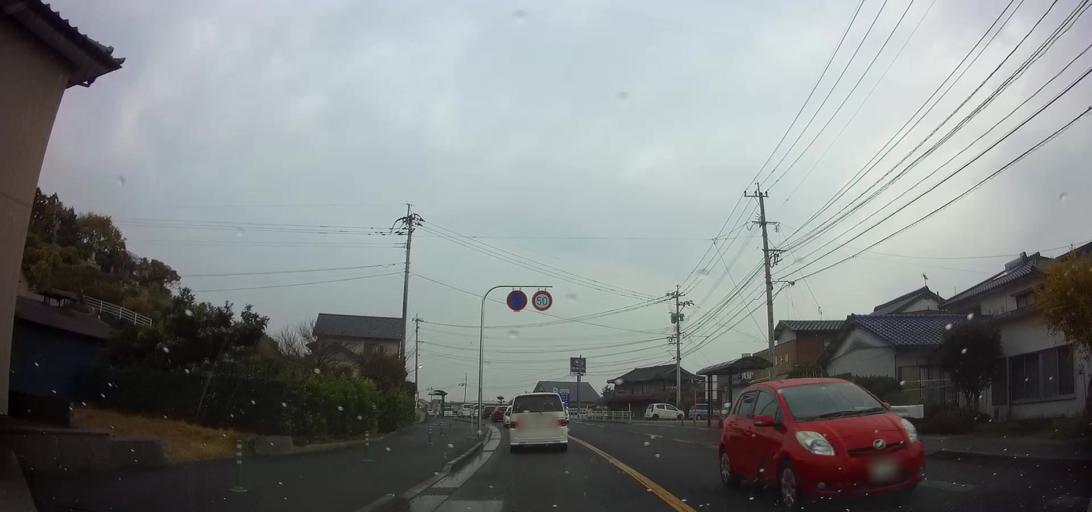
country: JP
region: Nagasaki
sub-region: Isahaya-shi
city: Isahaya
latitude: 32.8336
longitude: 130.1350
